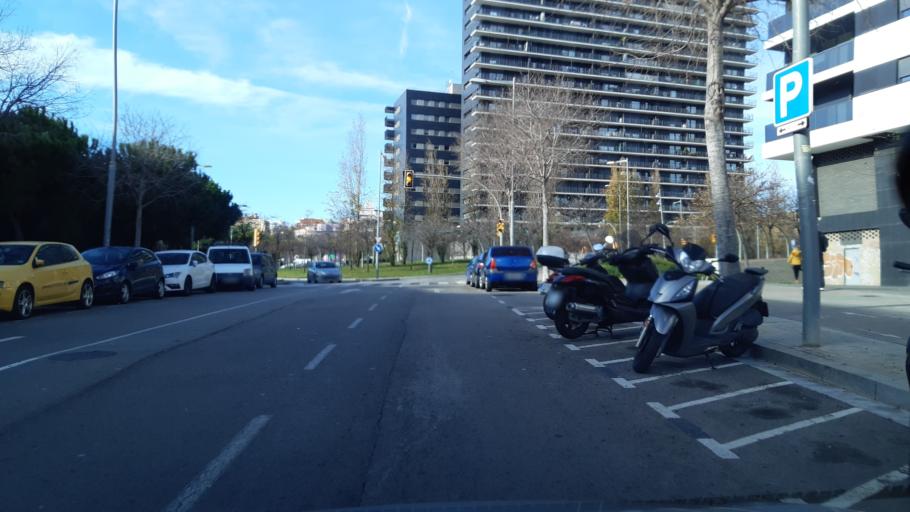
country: ES
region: Catalonia
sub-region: Provincia de Barcelona
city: L'Hospitalet de Llobregat
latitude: 41.3747
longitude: 2.1104
